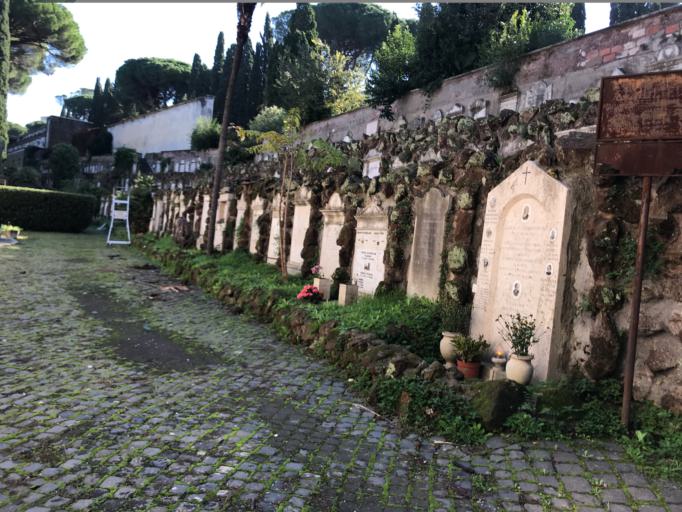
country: IT
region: Latium
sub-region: Citta metropolitana di Roma Capitale
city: Rome
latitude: 41.9004
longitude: 12.5253
